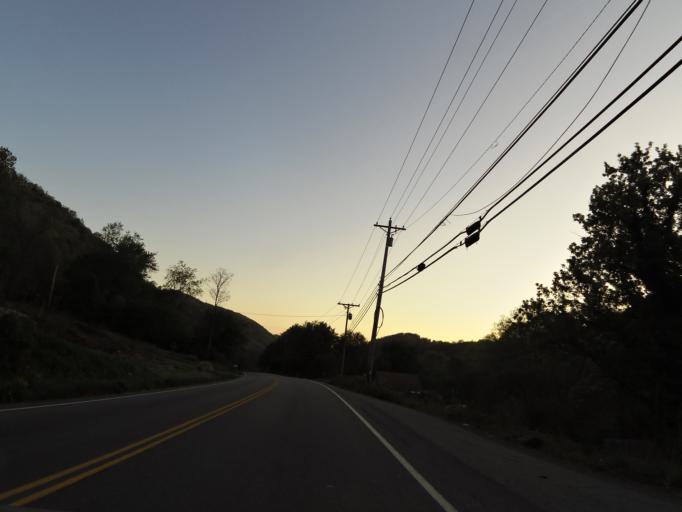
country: US
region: Tennessee
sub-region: Campbell County
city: LaFollette
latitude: 36.4007
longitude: -84.1215
